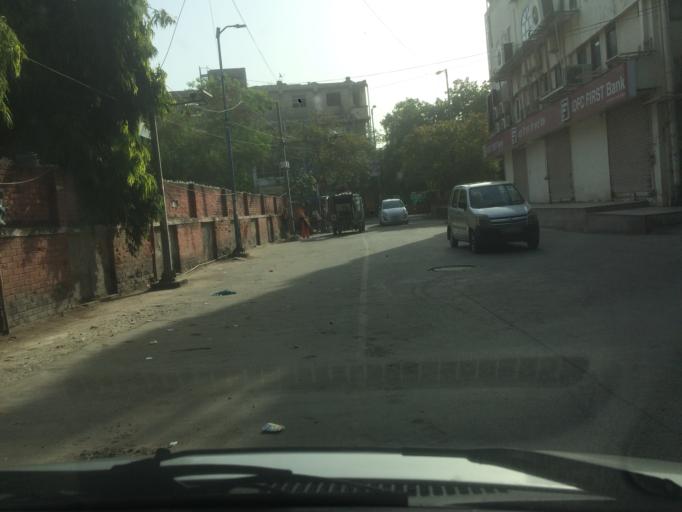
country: IN
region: Uttar Pradesh
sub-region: Gautam Buddha Nagar
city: Noida
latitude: 28.5627
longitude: 77.2685
